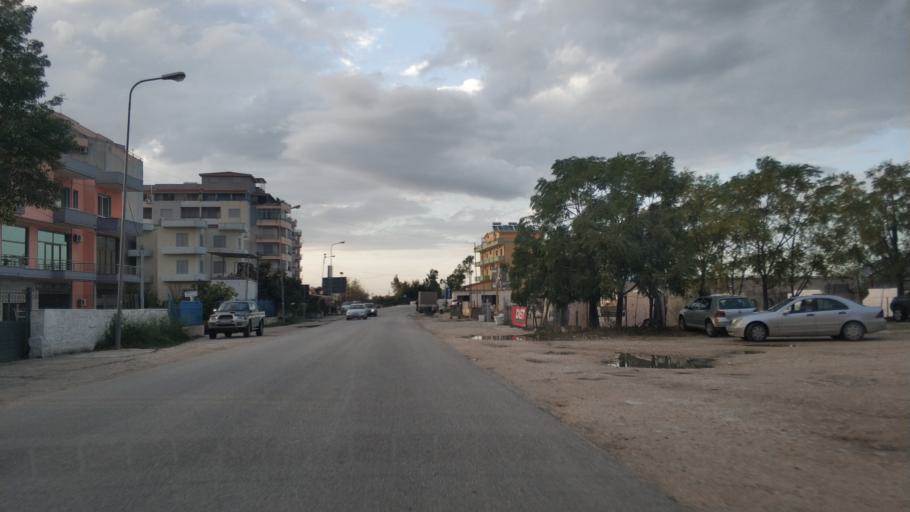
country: AL
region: Vlore
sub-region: Rrethi i Vlores
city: Orikum
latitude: 40.3304
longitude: 19.4770
